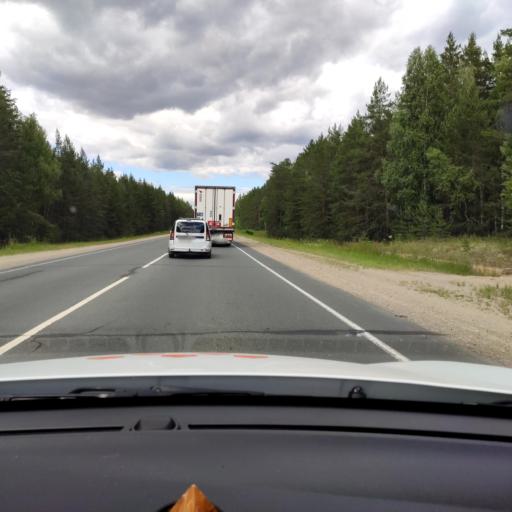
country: RU
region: Mariy-El
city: Krasnogorskiy
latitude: 56.1047
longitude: 48.3440
